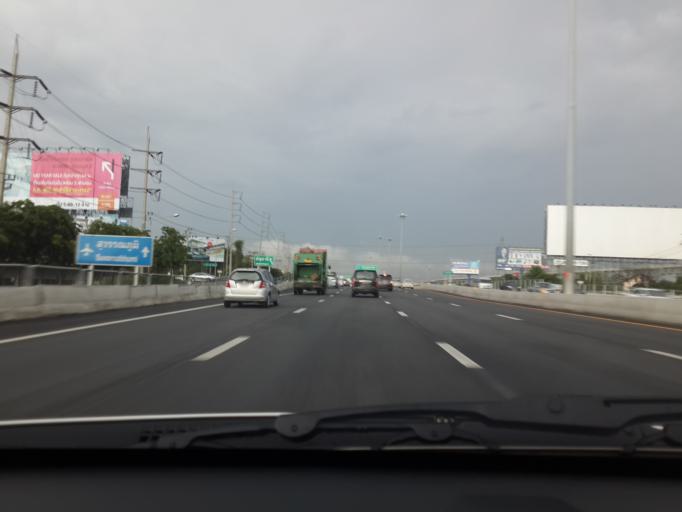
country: TH
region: Bangkok
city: Saphan Sung
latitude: 13.7337
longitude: 100.6941
